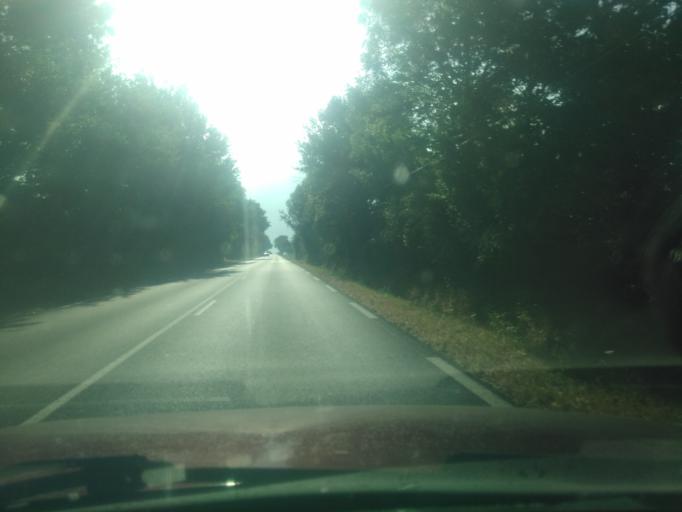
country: FR
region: Pays de la Loire
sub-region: Departement de la Vendee
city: Bazoges-en-Pareds
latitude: 46.6771
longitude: -0.8942
